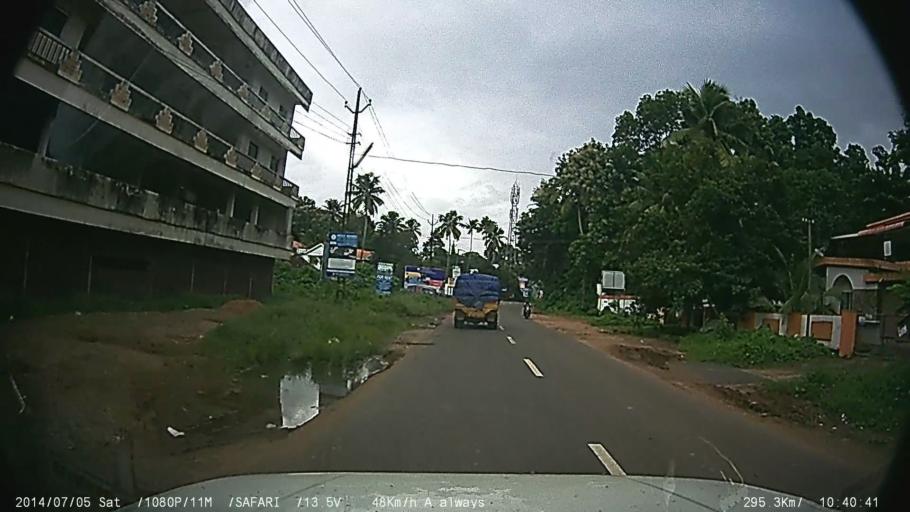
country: IN
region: Kerala
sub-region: Ernakulam
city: Muvattupuzha
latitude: 9.9736
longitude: 76.5802
